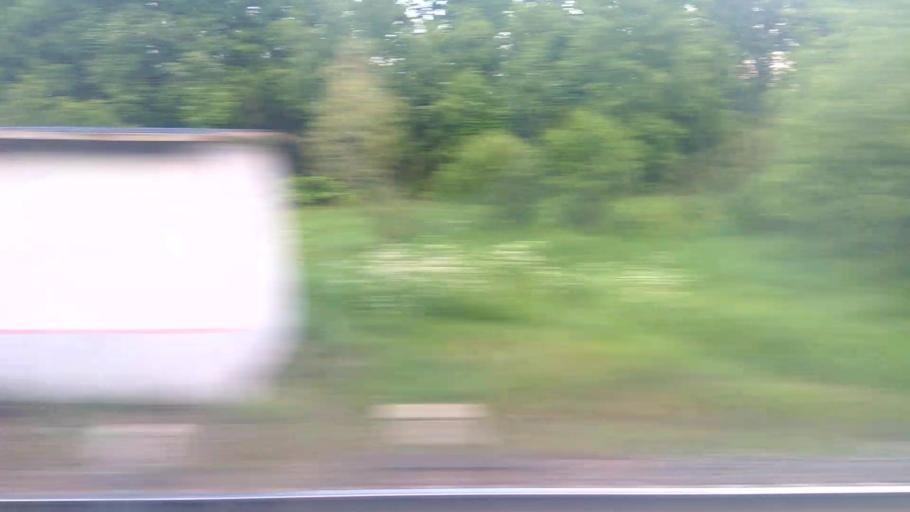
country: RU
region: Moskovskaya
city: Zhilevo
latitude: 55.0678
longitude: 37.9847
